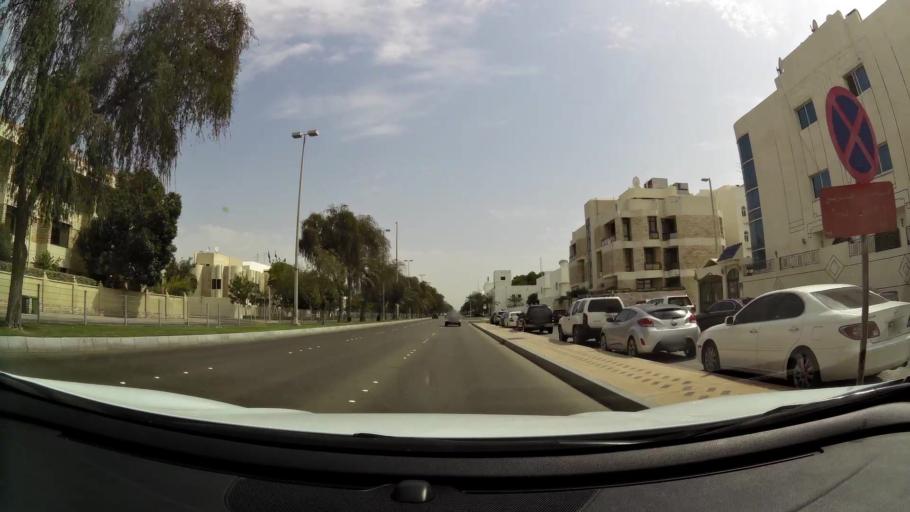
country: AE
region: Abu Dhabi
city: Abu Dhabi
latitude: 24.4576
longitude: 54.3650
